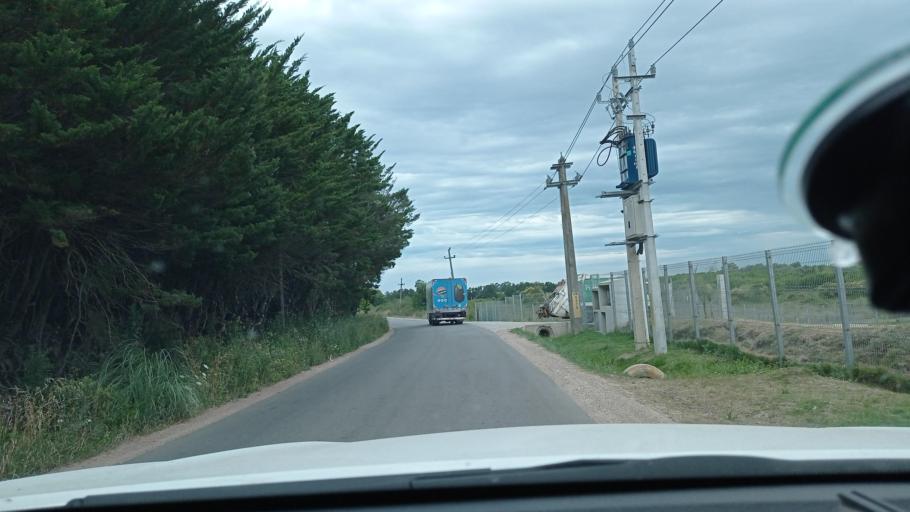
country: UY
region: Canelones
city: La Paz
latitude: -34.7993
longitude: -56.1934
